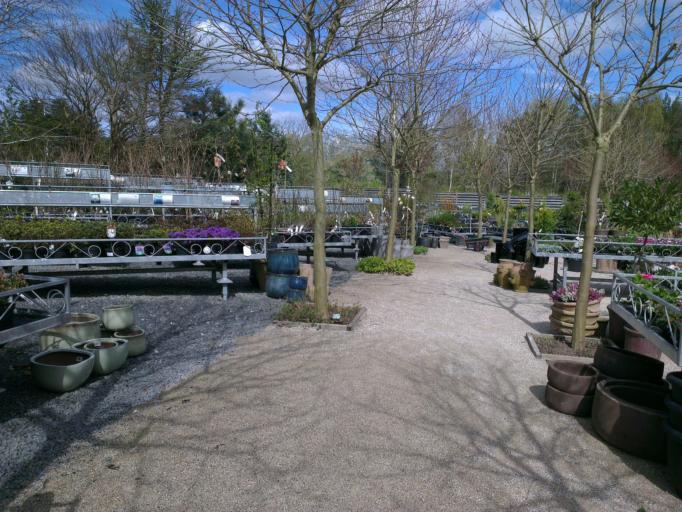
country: DK
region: Capital Region
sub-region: Frederikssund Kommune
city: Frederikssund
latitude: 55.8445
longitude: 12.0923
